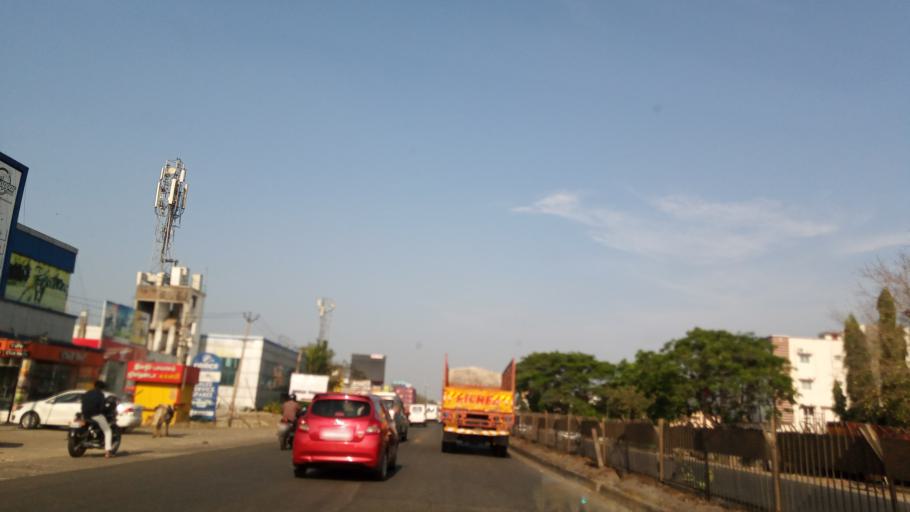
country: IN
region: Tamil Nadu
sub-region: Kancheepuram
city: Poonamalle
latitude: 13.0470
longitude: 80.0755
